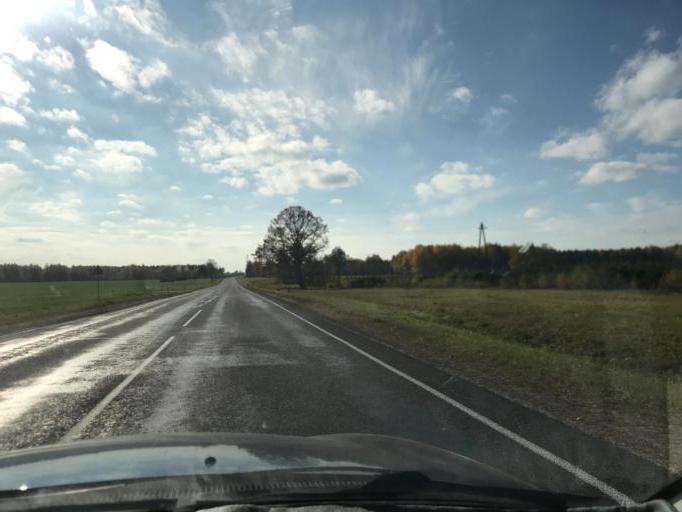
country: BY
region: Grodnenskaya
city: Voranava
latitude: 54.1819
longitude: 25.3356
